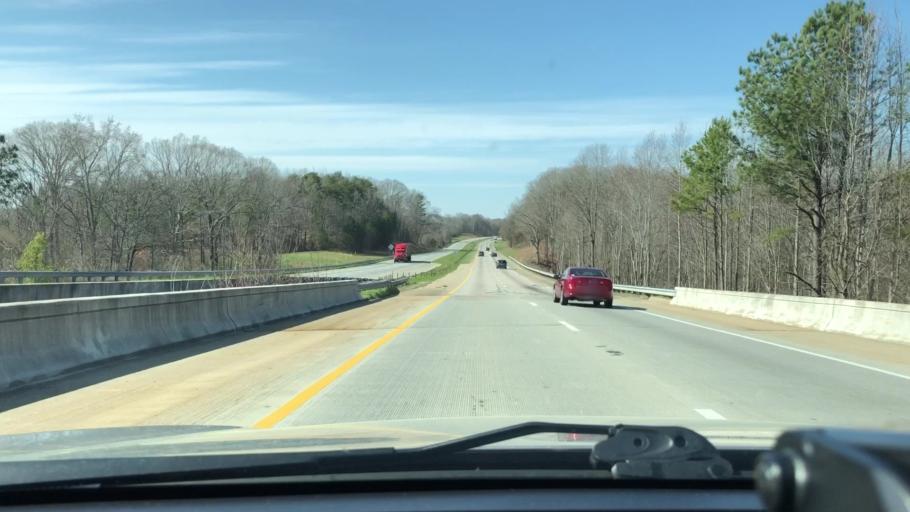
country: US
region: South Carolina
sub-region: Spartanburg County
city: Roebuck
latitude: 34.8606
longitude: -81.9817
